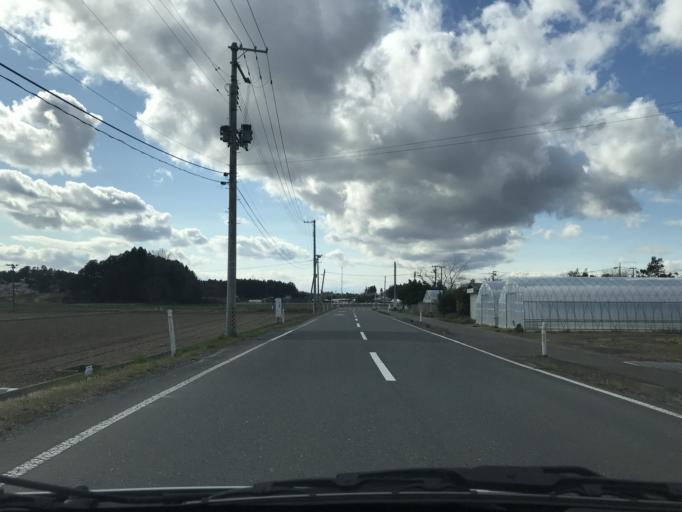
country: JP
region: Miyagi
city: Wakuya
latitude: 38.6571
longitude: 141.1984
